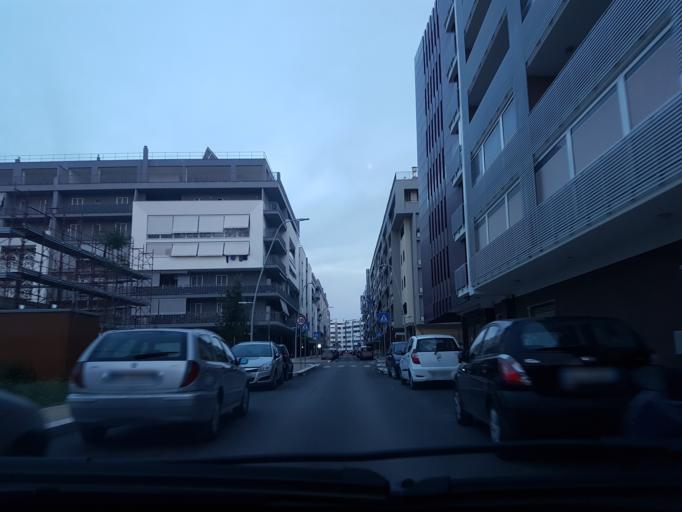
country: IT
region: Apulia
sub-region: Provincia di Barletta - Andria - Trani
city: Barletta
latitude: 41.3059
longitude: 16.2650
